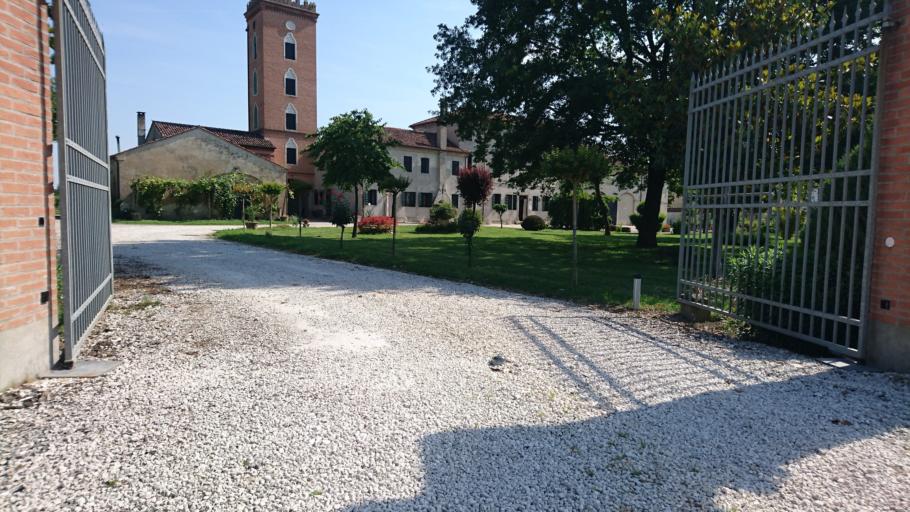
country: IT
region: Veneto
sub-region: Provincia di Padova
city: Casale di Scodosia
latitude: 45.1801
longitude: 11.4790
